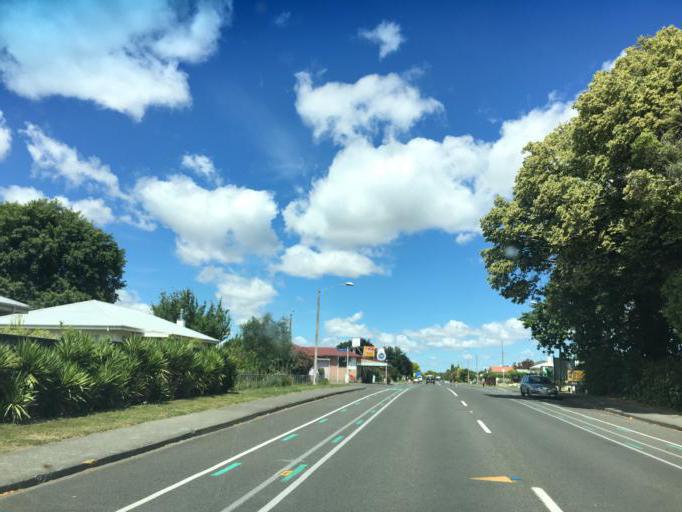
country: NZ
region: Hawke's Bay
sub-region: Hastings District
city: Hastings
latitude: -39.6491
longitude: 176.8615
